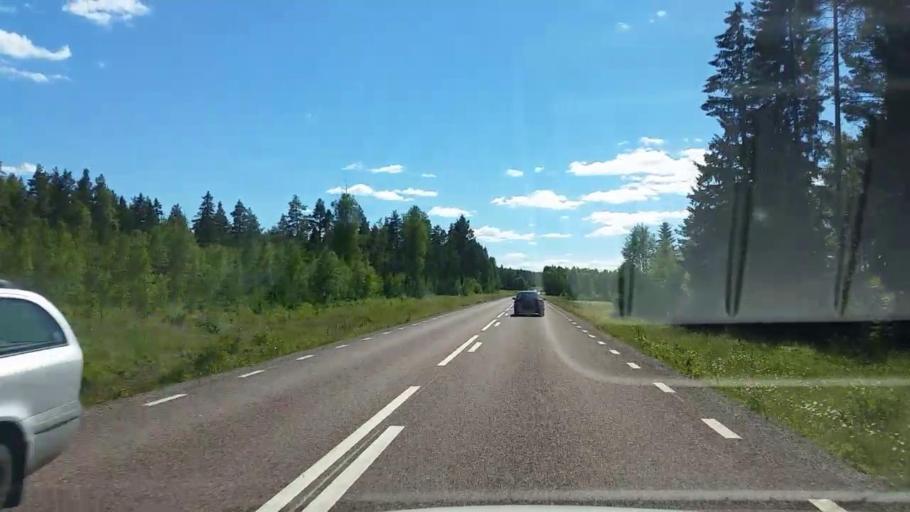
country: SE
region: Gaevleborg
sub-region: Ovanakers Kommun
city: Edsbyn
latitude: 61.2763
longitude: 15.8953
